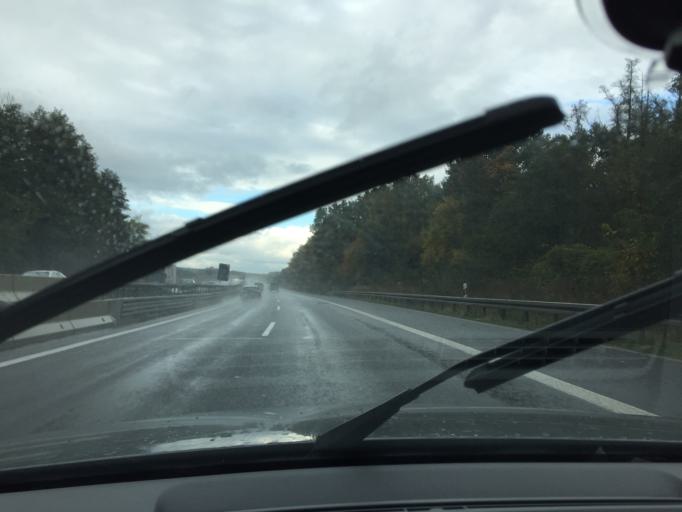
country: DE
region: Saxony
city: Radeburg
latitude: 51.2190
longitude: 13.7342
